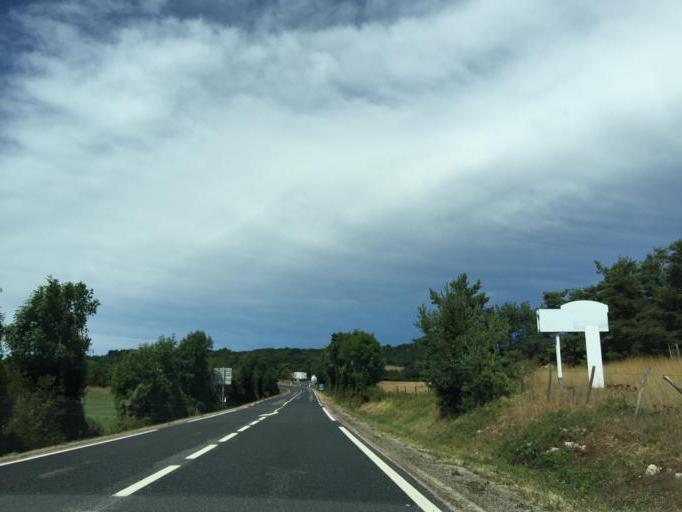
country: FR
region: Midi-Pyrenees
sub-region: Departement de l'Aveyron
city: Severac-le-Chateau
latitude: 44.2227
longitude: 2.9947
